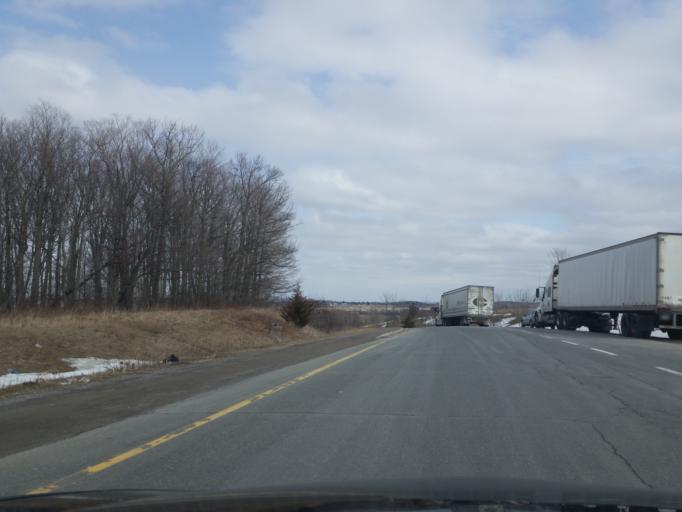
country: CA
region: Ontario
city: Cobourg
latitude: 43.9526
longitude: -78.3864
